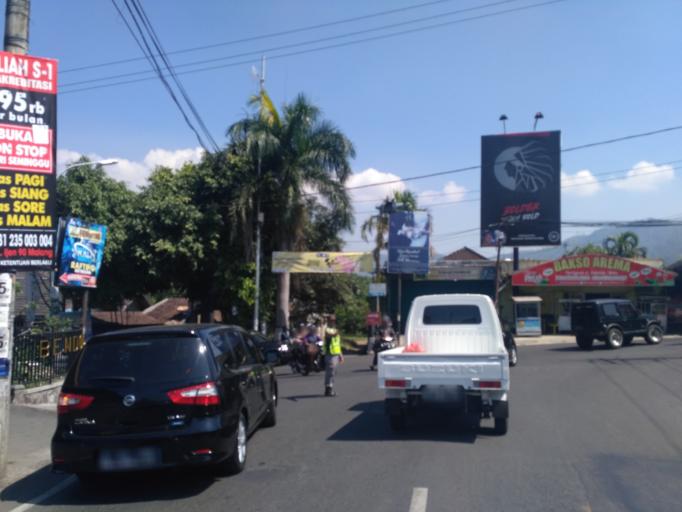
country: ID
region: East Java
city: Batu
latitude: -7.8630
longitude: 112.5271
